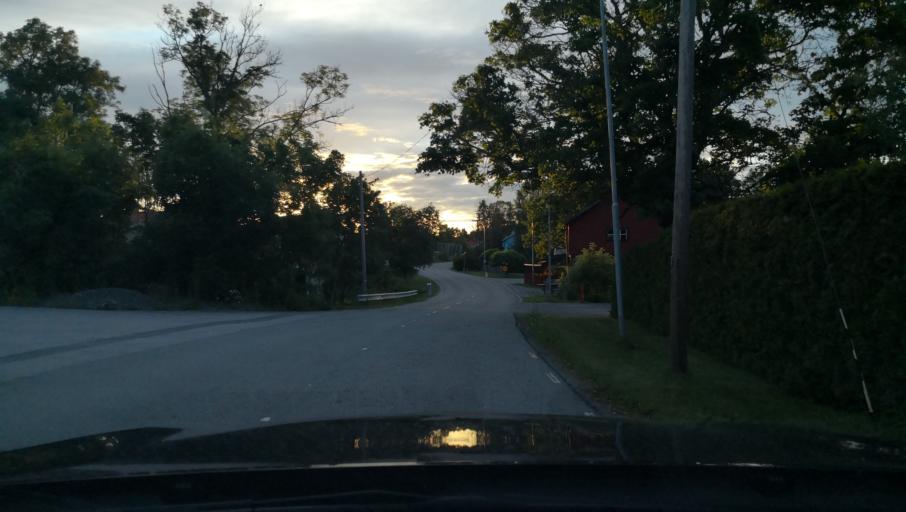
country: SE
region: Uppsala
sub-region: Enkopings Kommun
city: Grillby
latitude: 59.6575
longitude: 17.2462
